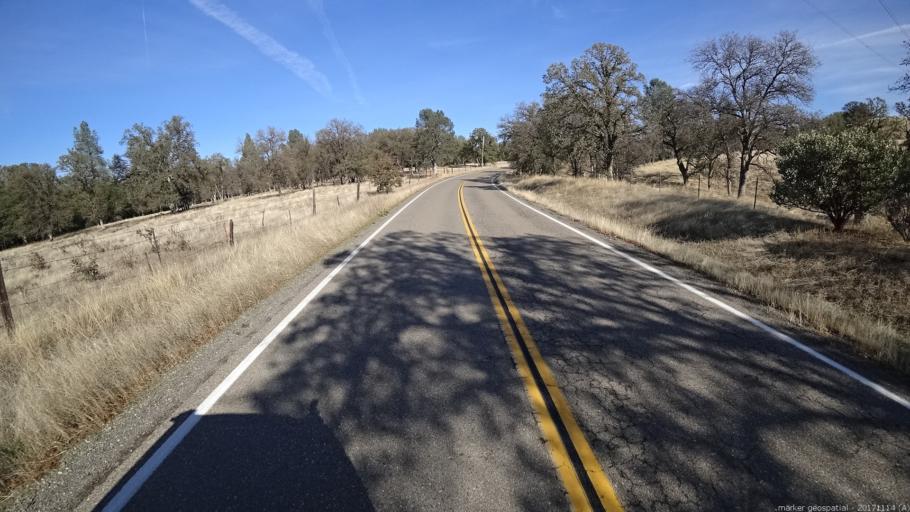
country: US
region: California
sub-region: Shasta County
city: Anderson
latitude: 40.4054
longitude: -122.3545
